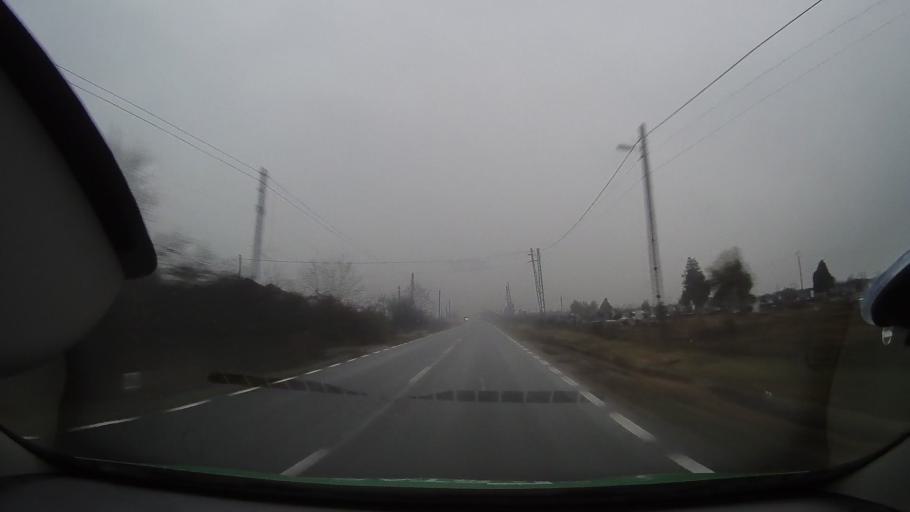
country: RO
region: Bihor
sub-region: Comuna Tinca
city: Tinca
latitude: 46.7355
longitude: 21.9418
